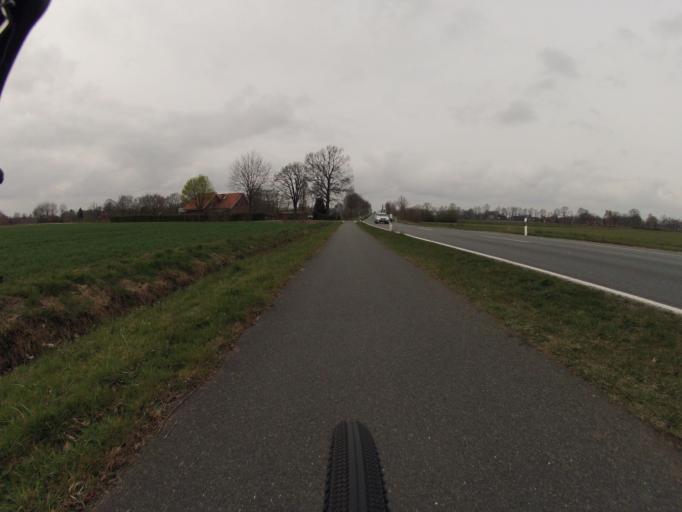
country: DE
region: North Rhine-Westphalia
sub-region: Regierungsbezirk Munster
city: Recke
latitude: 52.3537
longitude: 7.7256
